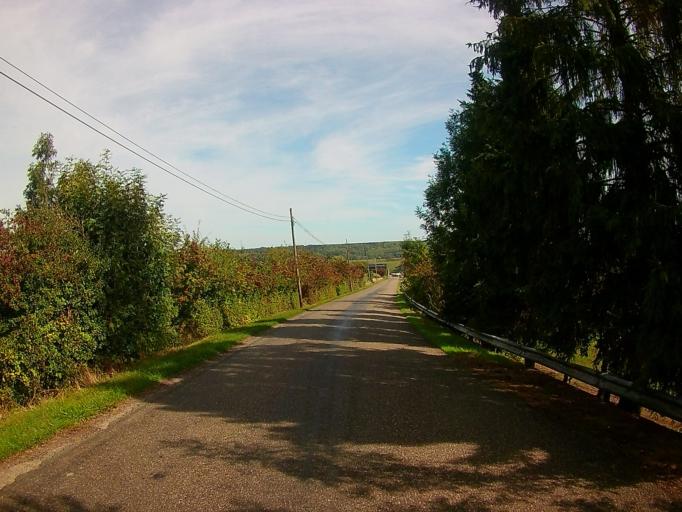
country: BE
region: Wallonia
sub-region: Province de Liege
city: Aubel
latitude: 50.7268
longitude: 5.8720
